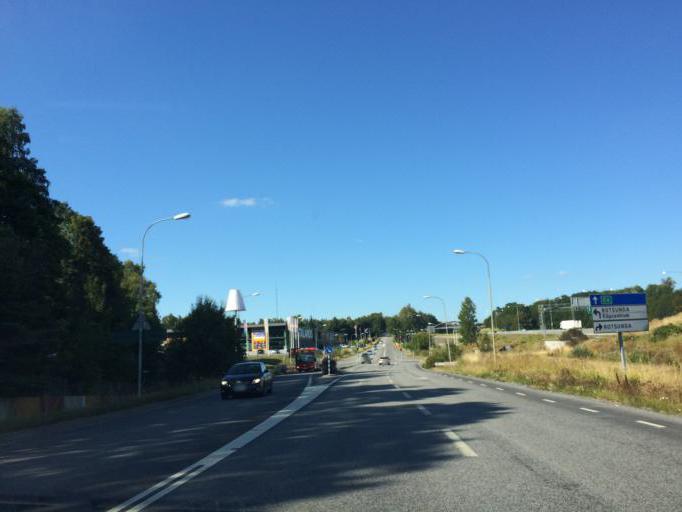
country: SE
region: Stockholm
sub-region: Upplands Vasby Kommun
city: Upplands Vaesby
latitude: 59.4821
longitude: 17.9187
